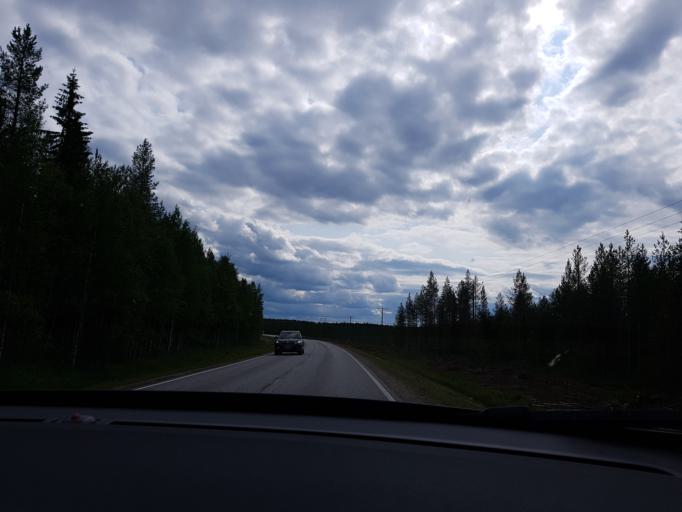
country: FI
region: Kainuu
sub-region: Kehys-Kainuu
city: Kuhmo
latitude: 64.2916
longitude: 29.8470
